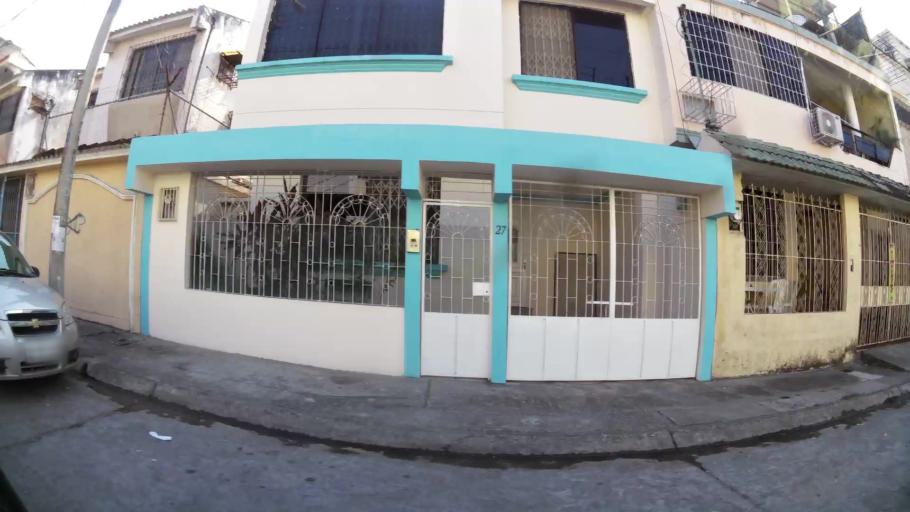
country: EC
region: Guayas
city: Guayaquil
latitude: -2.1517
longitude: -79.9115
